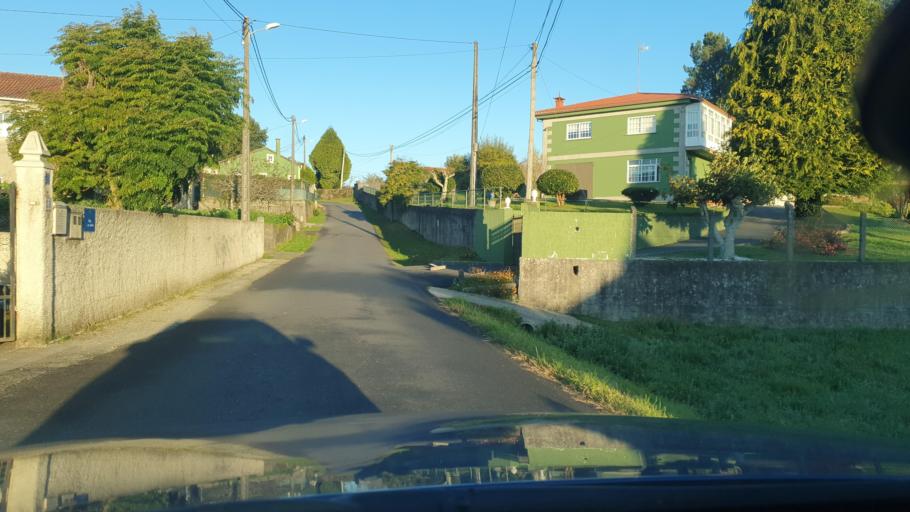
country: ES
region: Galicia
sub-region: Provincia da Coruna
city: Santiago de Compostela
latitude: 42.8327
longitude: -8.5997
